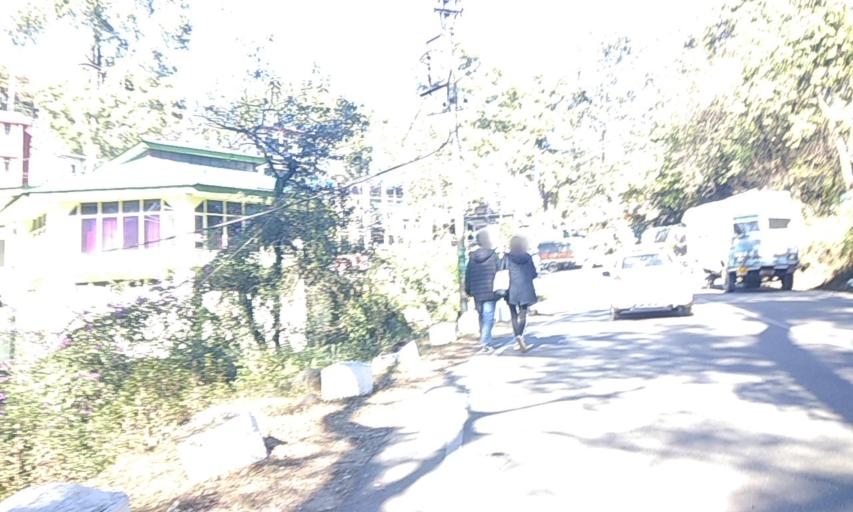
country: IN
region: Himachal Pradesh
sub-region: Kangra
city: Dharmsala
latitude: 32.2147
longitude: 76.3187
